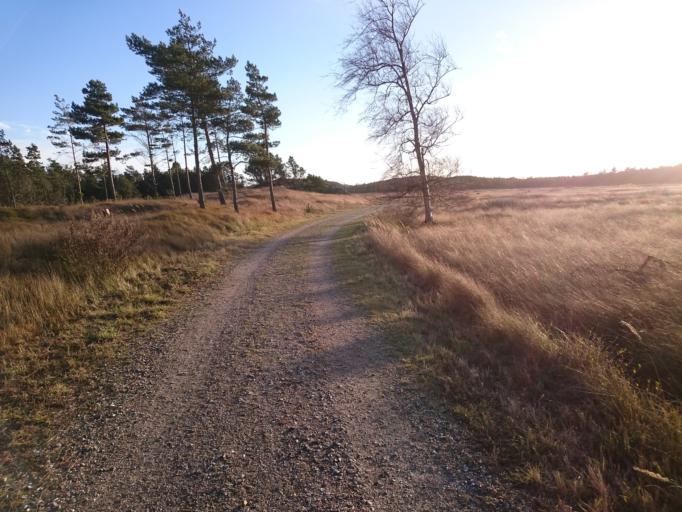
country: DK
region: North Denmark
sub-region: Frederikshavn Kommune
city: Skagen
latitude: 57.7120
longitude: 10.5457
